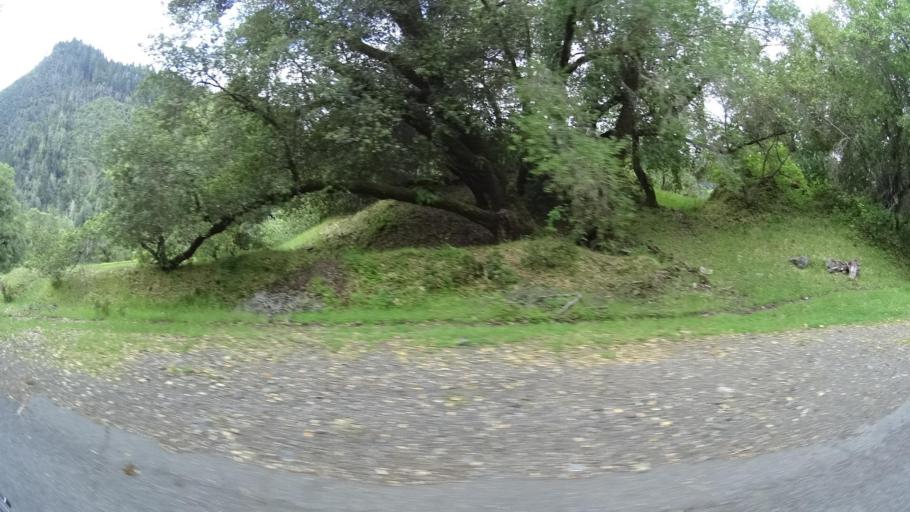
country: US
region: California
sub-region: Humboldt County
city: Redway
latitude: 40.2325
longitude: -123.6176
